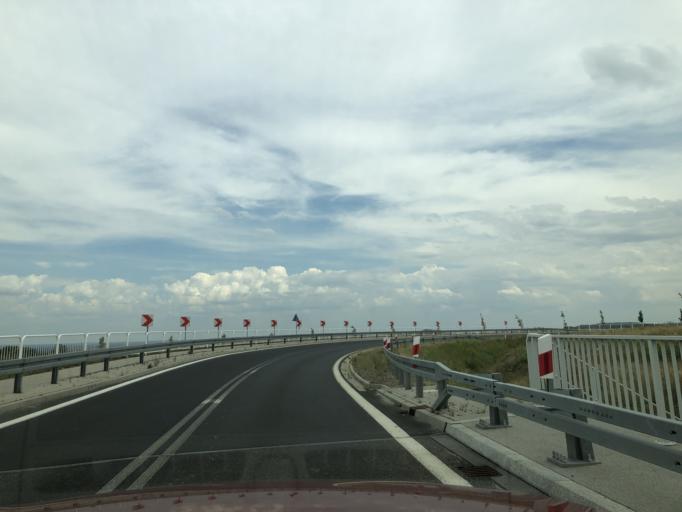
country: PL
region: Lower Silesian Voivodeship
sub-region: Powiat trzebnicki
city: Trzebnica
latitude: 51.3184
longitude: 17.0364
